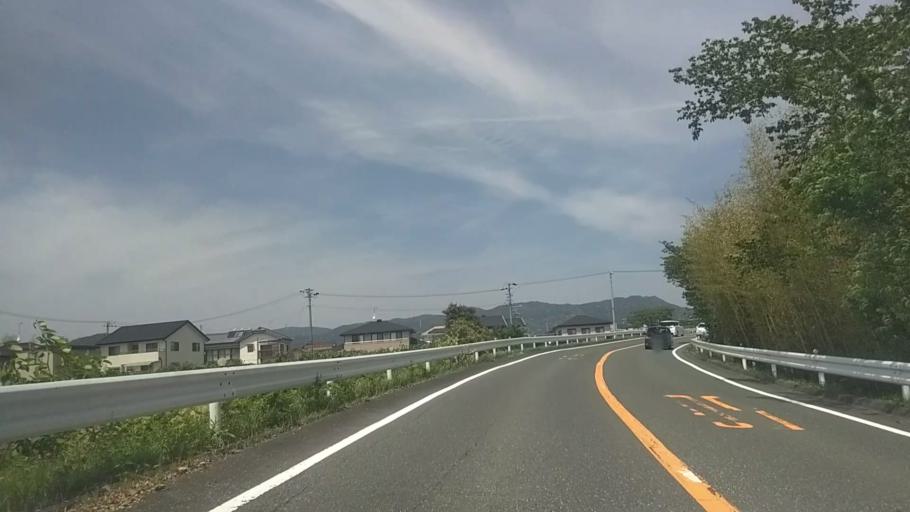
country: JP
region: Shizuoka
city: Kosai-shi
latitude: 34.7859
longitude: 137.5797
